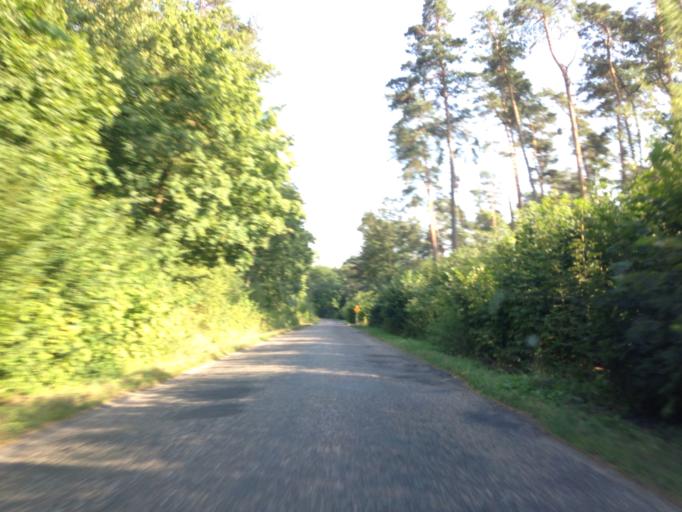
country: PL
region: Warmian-Masurian Voivodeship
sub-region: Powiat nowomiejski
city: Biskupiec
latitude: 53.4549
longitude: 19.2847
